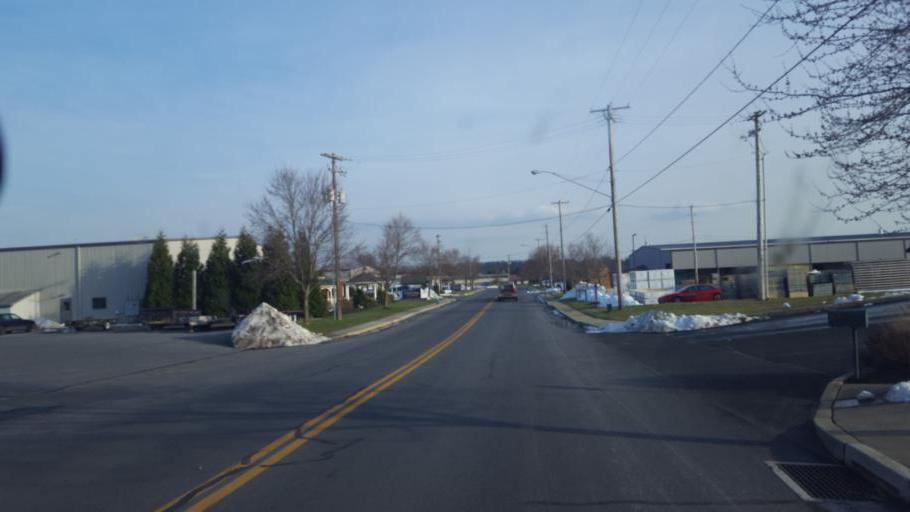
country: US
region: Pennsylvania
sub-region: Lancaster County
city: New Holland
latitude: 40.0915
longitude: -76.0890
